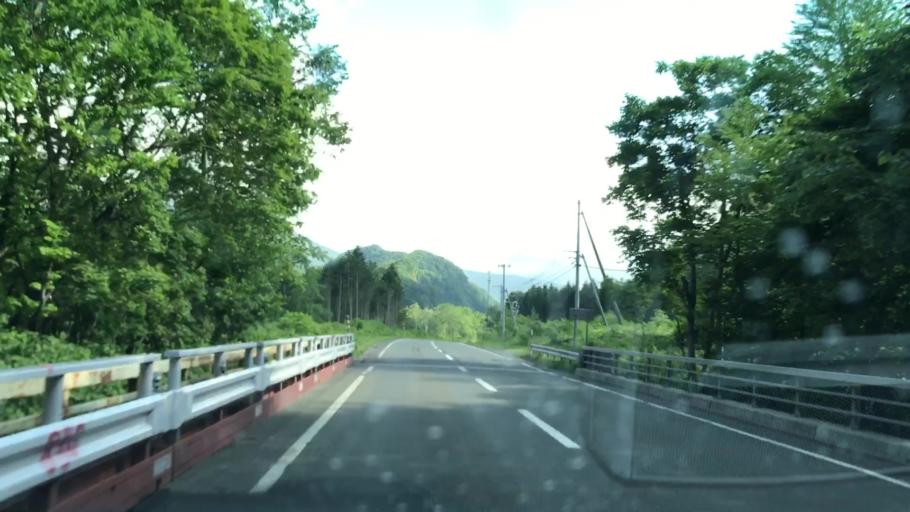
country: JP
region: Hokkaido
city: Shimo-furano
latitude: 42.8482
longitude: 142.4166
